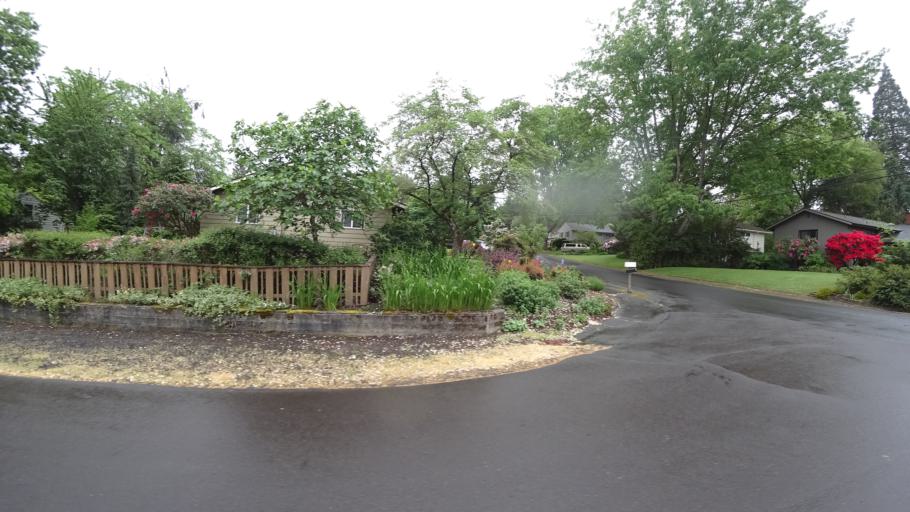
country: US
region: Oregon
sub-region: Washington County
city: Raleigh Hills
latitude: 45.4782
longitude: -122.7693
